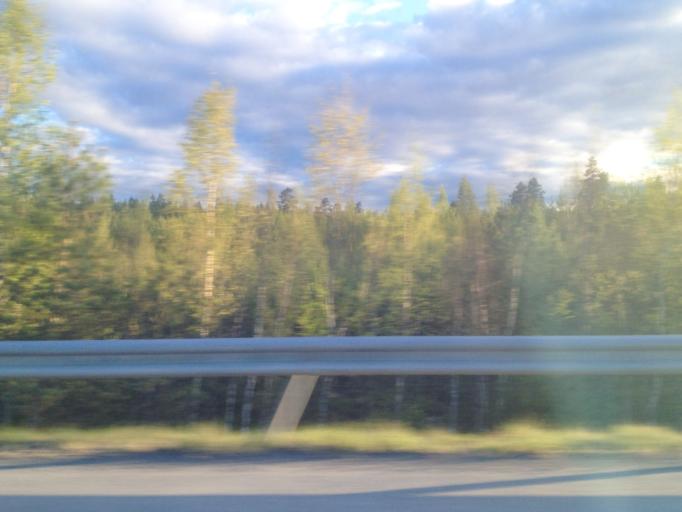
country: FI
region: Haeme
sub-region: Haemeenlinna
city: Kalvola
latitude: 61.1243
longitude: 24.1180
